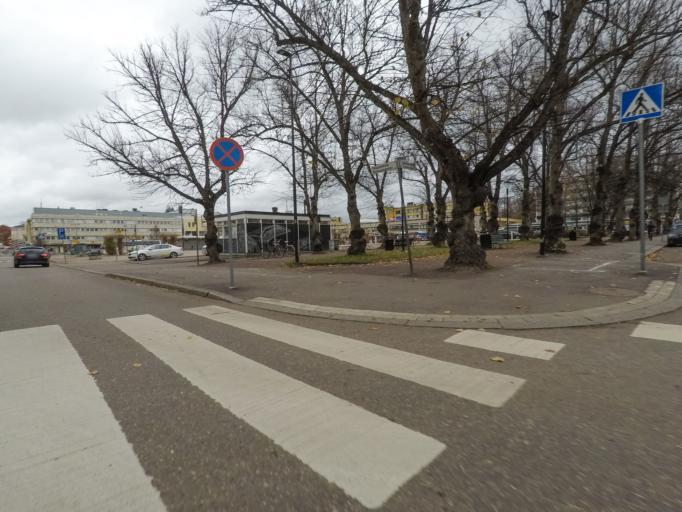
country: FI
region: Uusimaa
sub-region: Porvoo
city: Porvoo
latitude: 60.3922
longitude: 25.6642
